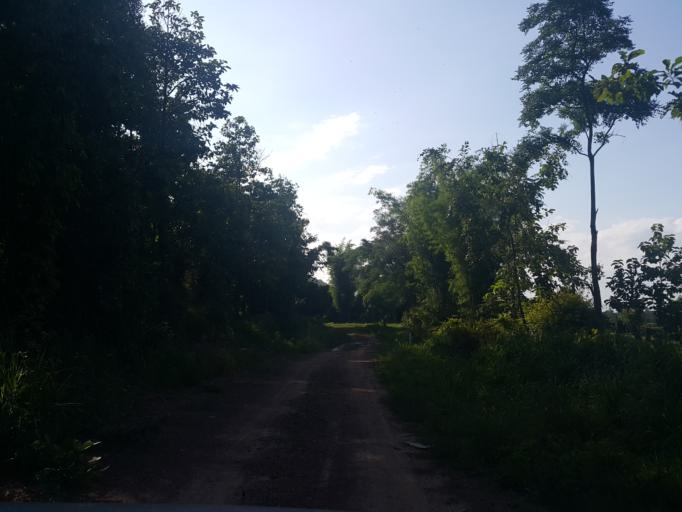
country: TH
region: Chiang Mai
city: Mae On
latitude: 18.7129
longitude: 99.2066
